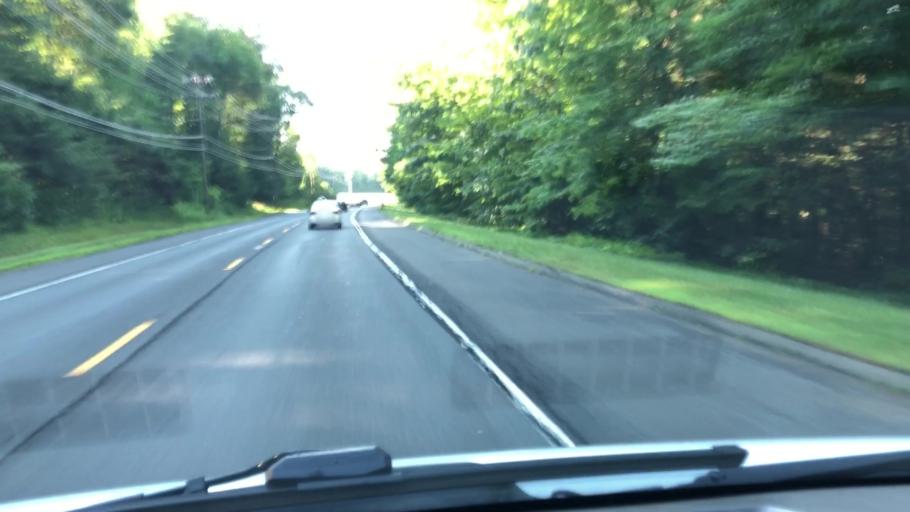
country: US
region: Massachusetts
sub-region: Hampshire County
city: North Amherst
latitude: 42.4398
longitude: -72.5490
